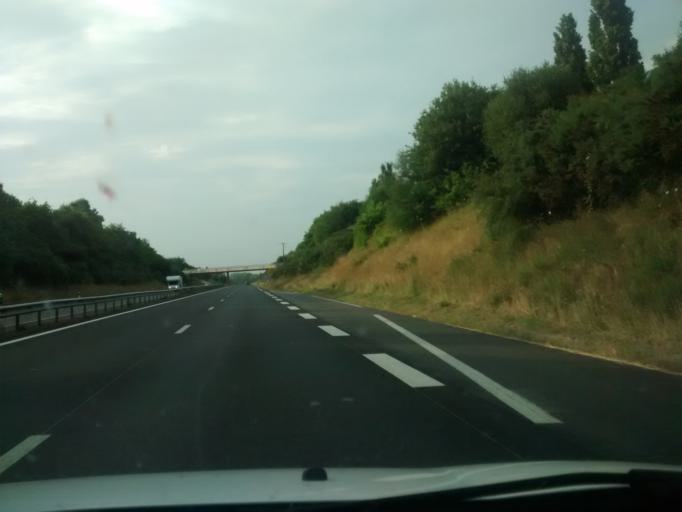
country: FR
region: Brittany
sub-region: Departement des Cotes-d'Armor
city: Cavan
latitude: 48.6726
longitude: -3.3519
